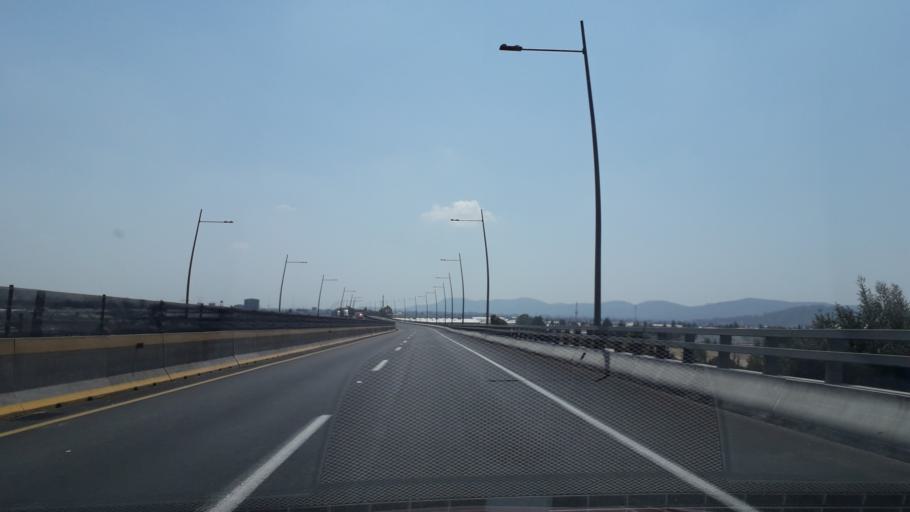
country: MX
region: Puebla
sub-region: Puebla
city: San Sebastian de Aparicio
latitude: 19.0806
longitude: -98.1620
